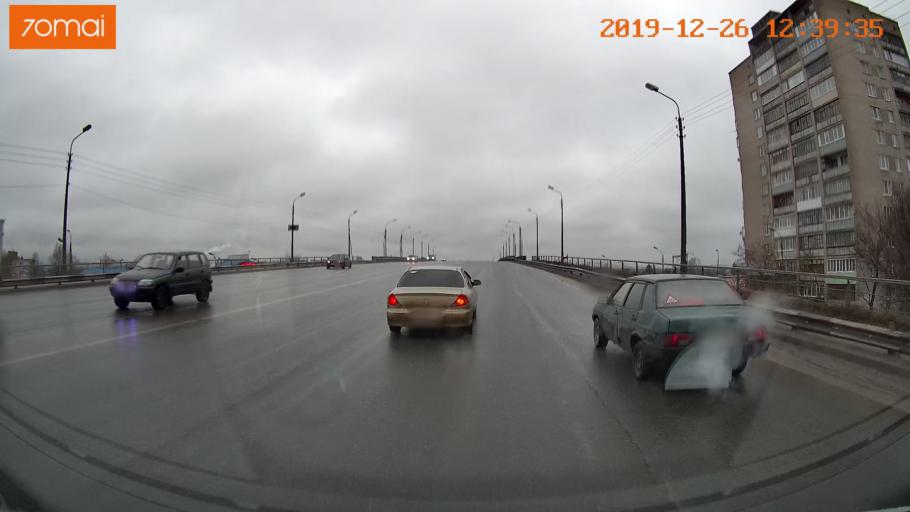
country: RU
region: Vologda
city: Tonshalovo
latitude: 59.1347
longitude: 37.9782
